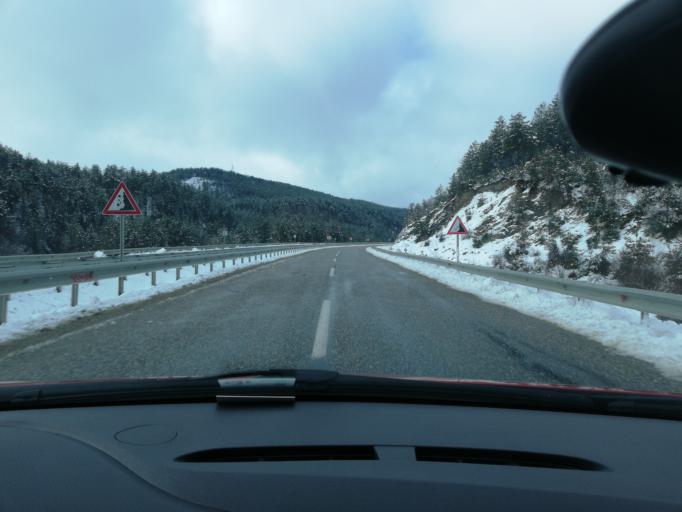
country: TR
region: Kastamonu
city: Akkaya
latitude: 41.2821
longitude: 33.4299
